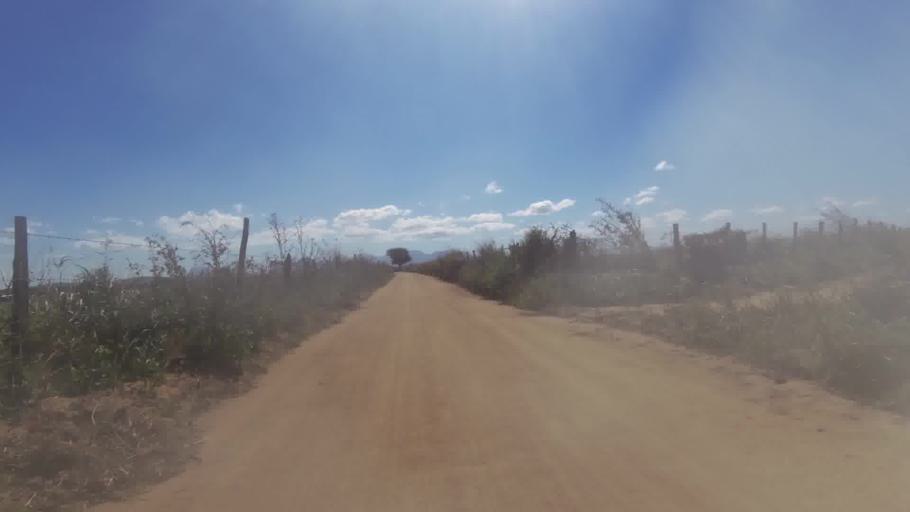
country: BR
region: Espirito Santo
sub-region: Marataizes
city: Marataizes
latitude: -21.1554
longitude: -40.9668
